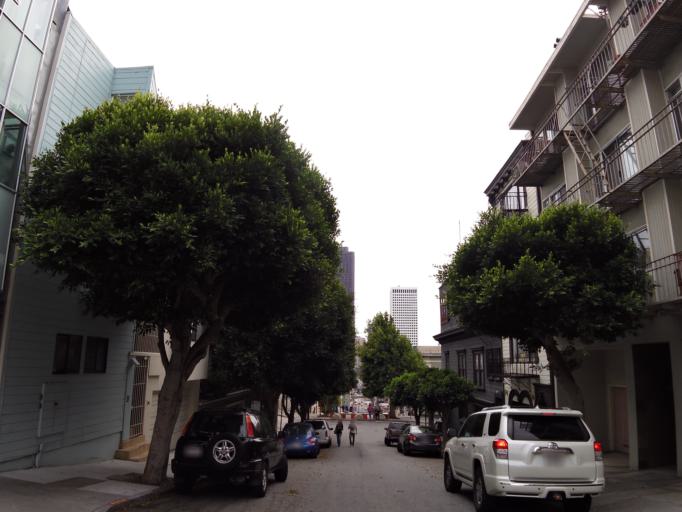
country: US
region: California
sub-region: San Francisco County
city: San Francisco
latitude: 37.7995
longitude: -122.4058
